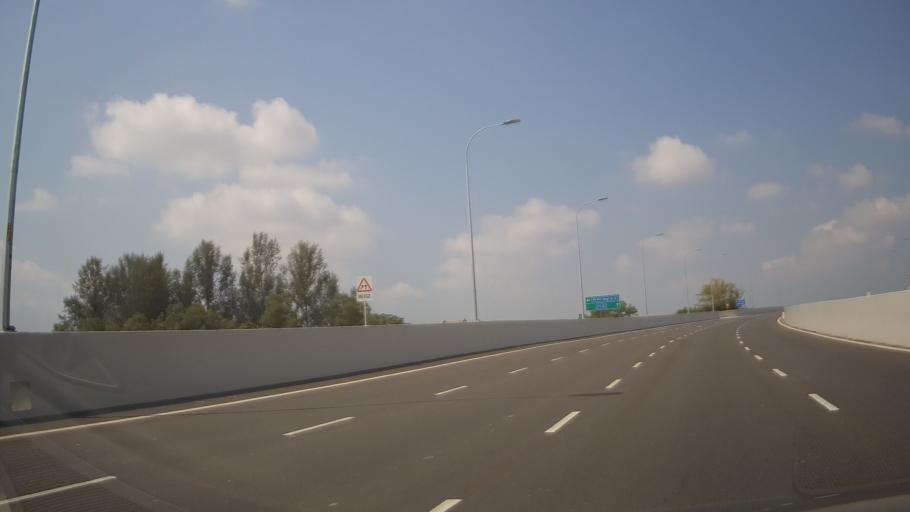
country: MY
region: Johor
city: Kampung Pasir Gudang Baru
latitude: 1.3869
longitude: 103.9224
